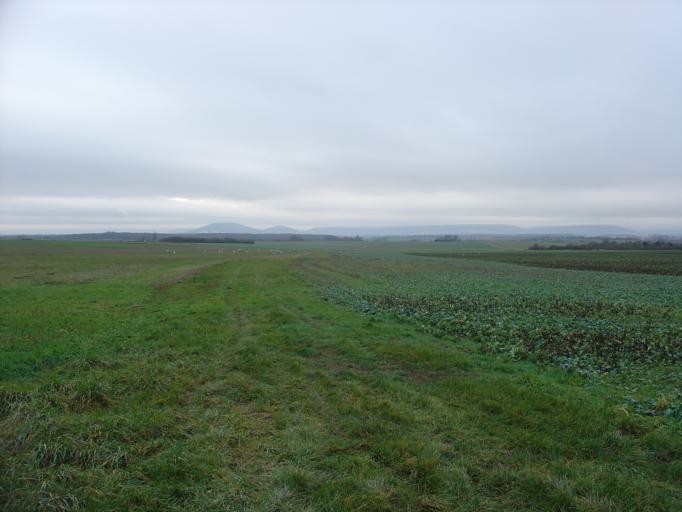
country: FR
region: Lorraine
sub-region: Departement de Meurthe-et-Moselle
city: Villey-Saint-Etienne
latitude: 48.7412
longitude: 5.9740
